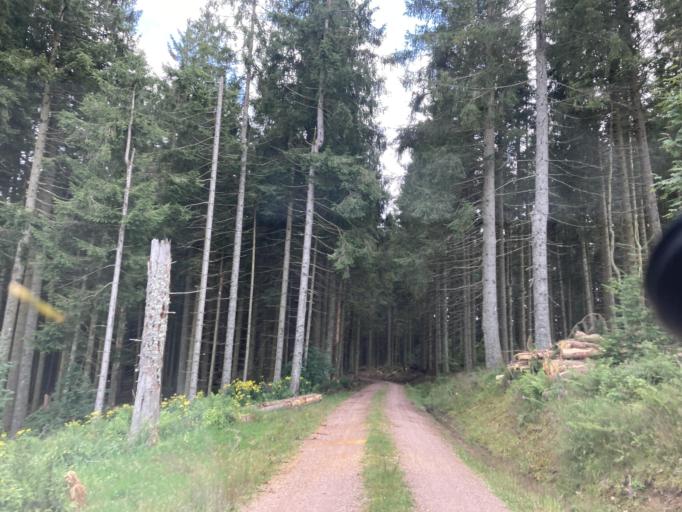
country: DE
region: Baden-Wuerttemberg
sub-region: Freiburg Region
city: Schonach im Schwarzwald
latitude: 48.1516
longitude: 8.1413
